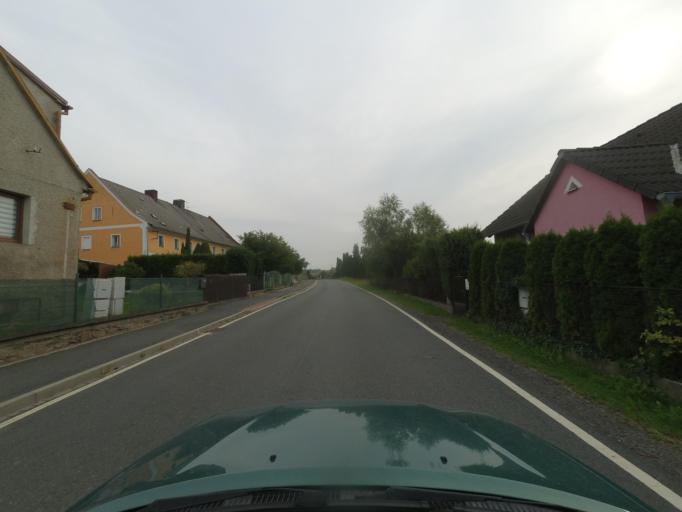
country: CZ
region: Plzensky
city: Bela nad Radbuzou
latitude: 49.5912
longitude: 12.7035
